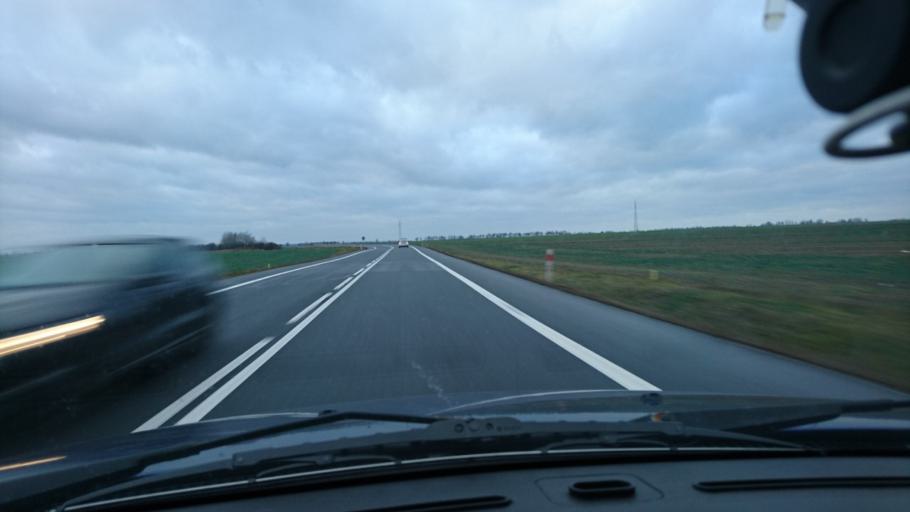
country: PL
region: Opole Voivodeship
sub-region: Powiat kluczborski
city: Kluczbork
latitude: 50.9870
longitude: 18.2375
